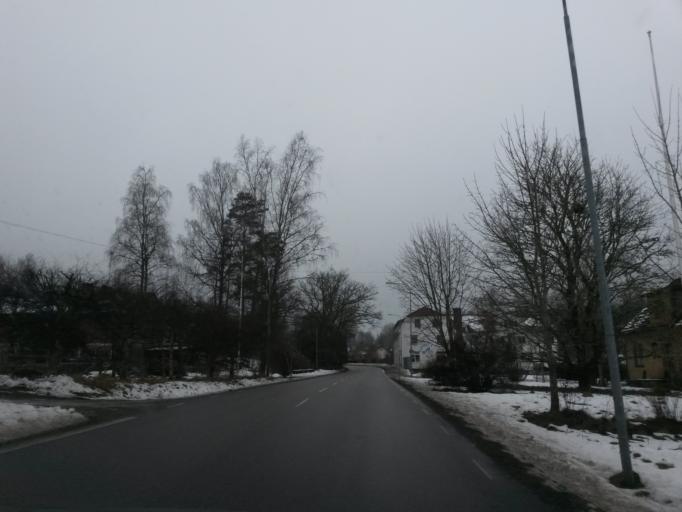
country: SE
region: Vaestra Goetaland
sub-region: Tranemo Kommun
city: Langhem
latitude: 57.6972
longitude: 13.3019
